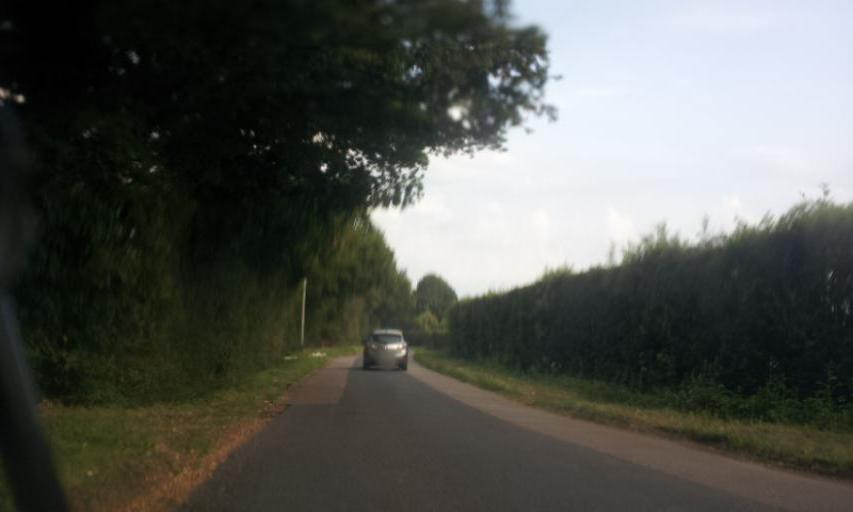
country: GB
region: England
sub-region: Kent
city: Paddock Wood
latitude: 51.1864
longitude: 0.4136
